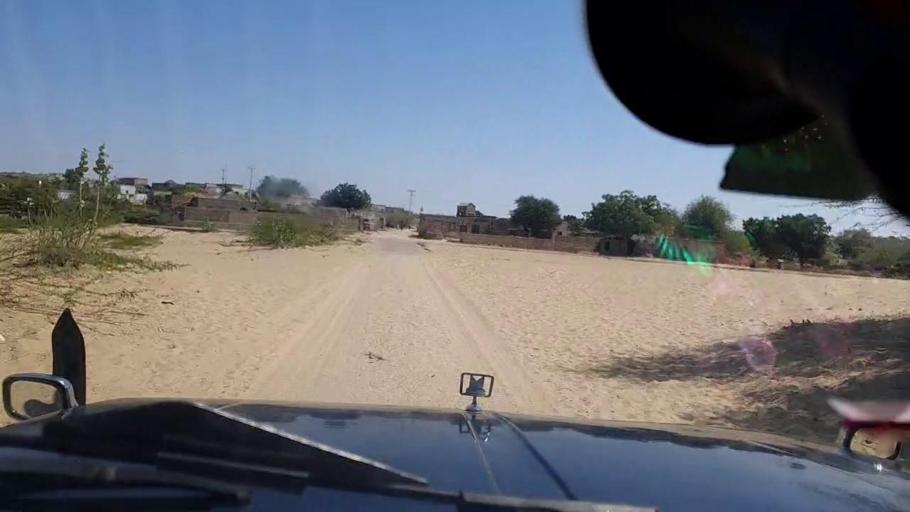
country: PK
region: Sindh
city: Diplo
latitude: 24.5679
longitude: 69.6801
